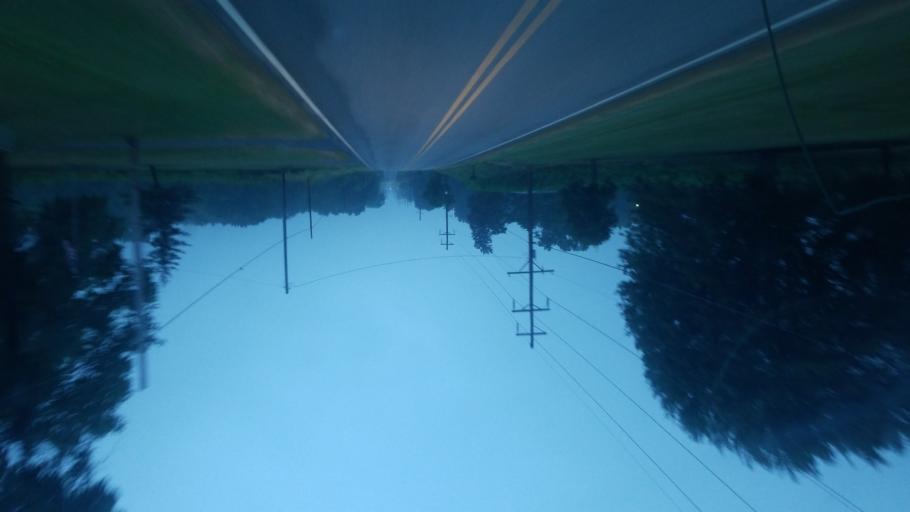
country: US
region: Ohio
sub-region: Defiance County
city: Hicksville
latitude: 41.3218
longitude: -84.7667
